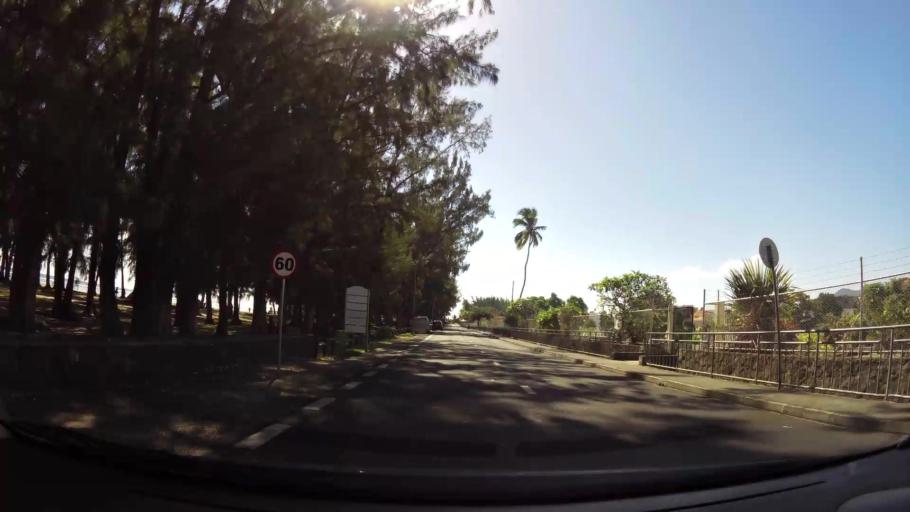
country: MU
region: Black River
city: Flic en Flac
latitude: -20.2825
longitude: 57.3653
